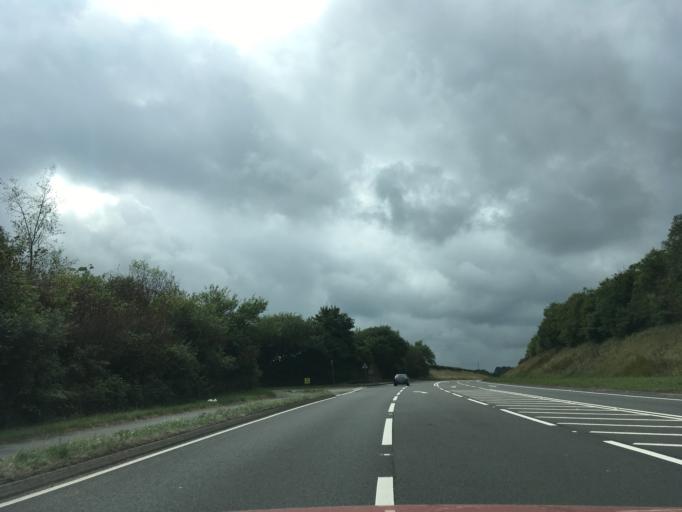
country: GB
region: Wales
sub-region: Carmarthenshire
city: Whitland
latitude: 51.8236
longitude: -4.5763
